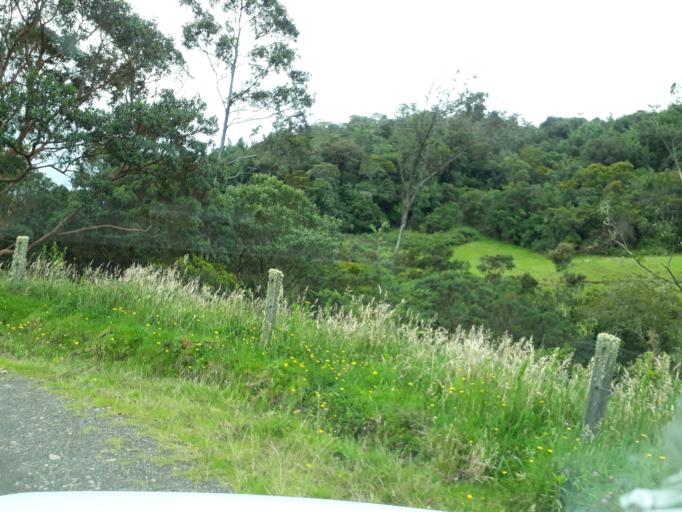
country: CO
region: Cundinamarca
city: Junin
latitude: 4.7453
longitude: -73.6268
